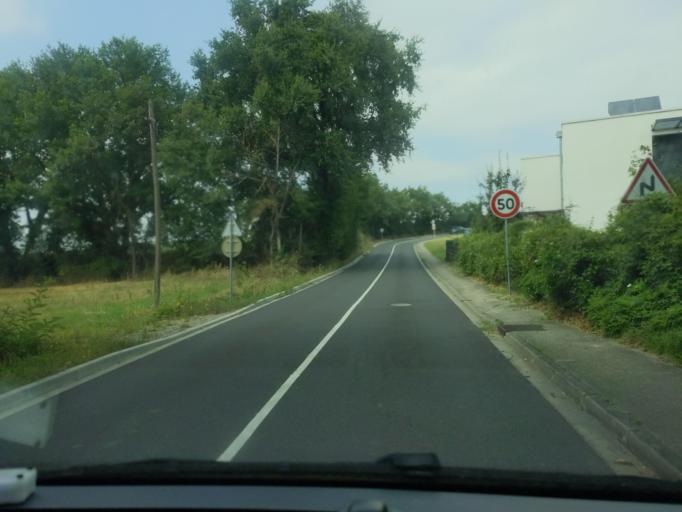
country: FR
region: Midi-Pyrenees
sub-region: Departement de la Haute-Garonne
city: Labege
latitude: 43.5398
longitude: 1.5316
